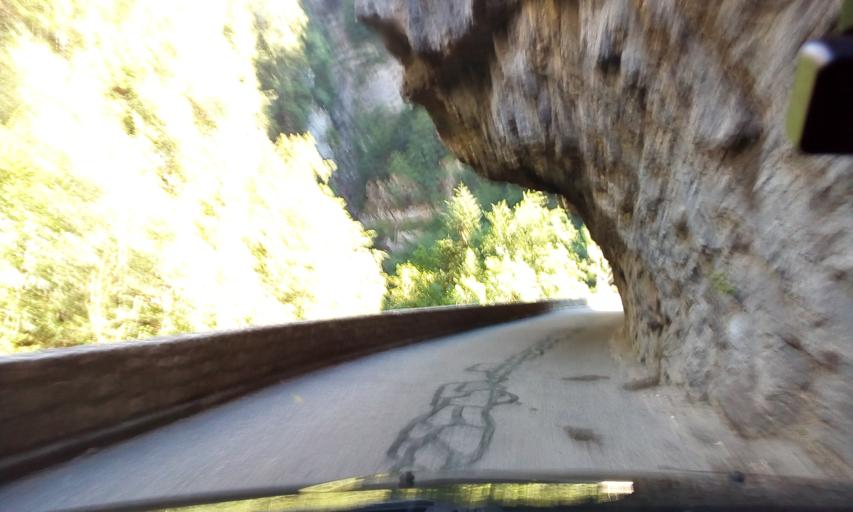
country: FR
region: Rhone-Alpes
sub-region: Departement de l'Isere
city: Villard-de-Lans
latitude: 45.0681
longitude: 5.5175
